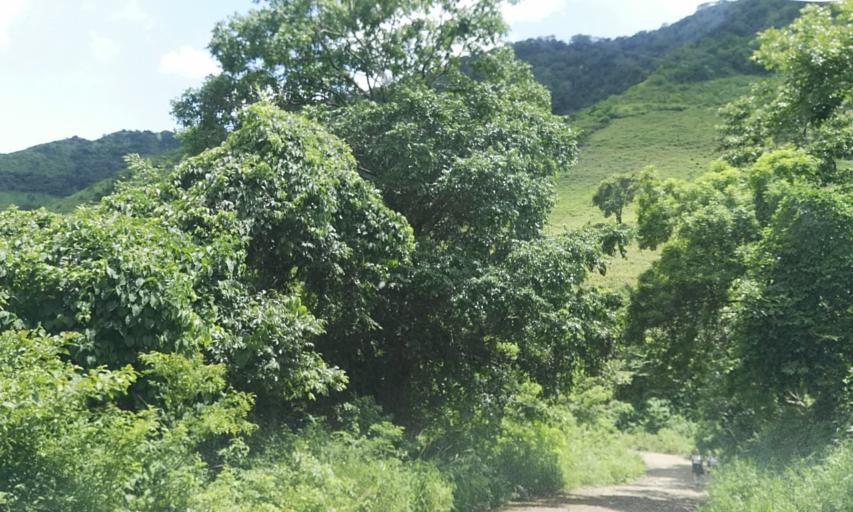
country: NI
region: Matagalpa
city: Terrabona
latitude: 12.7302
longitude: -85.9303
